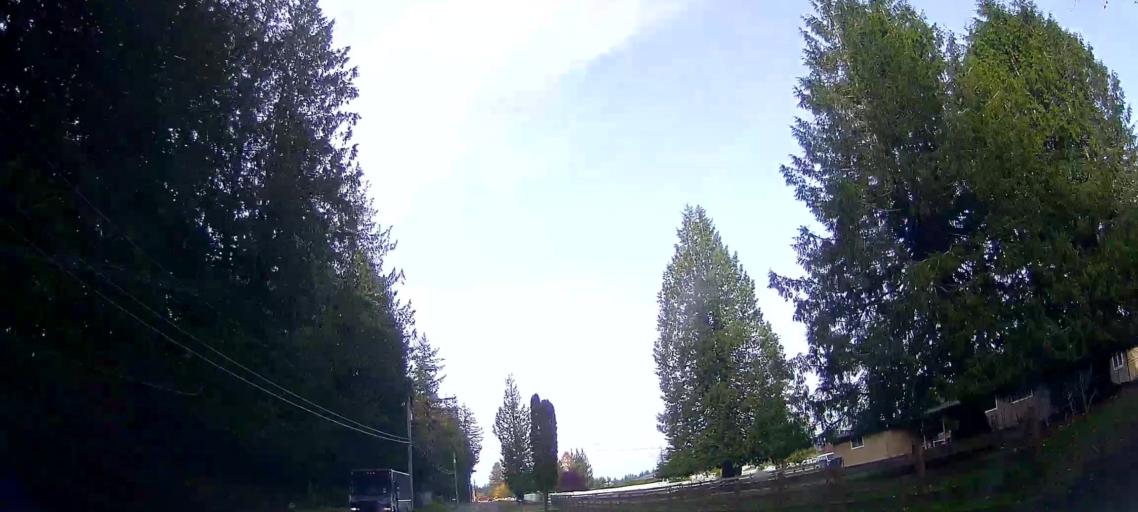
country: US
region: Washington
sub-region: Snohomish County
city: Stanwood
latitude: 48.2649
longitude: -122.3414
